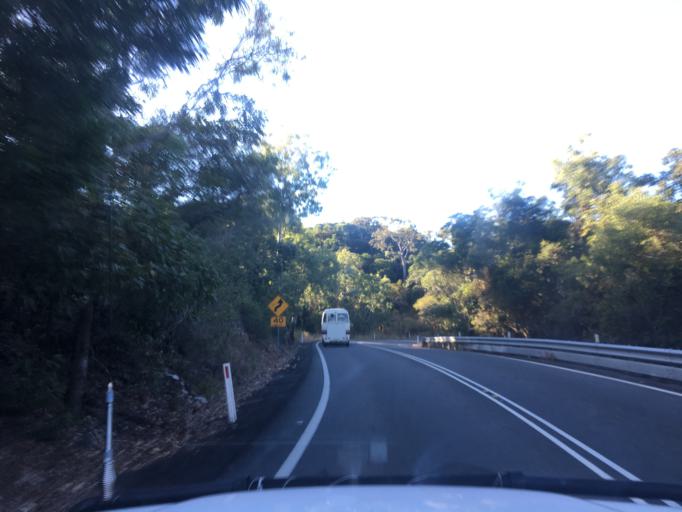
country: AU
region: Queensland
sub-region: Cairns
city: Palm Cove
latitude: -16.6517
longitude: 145.5646
